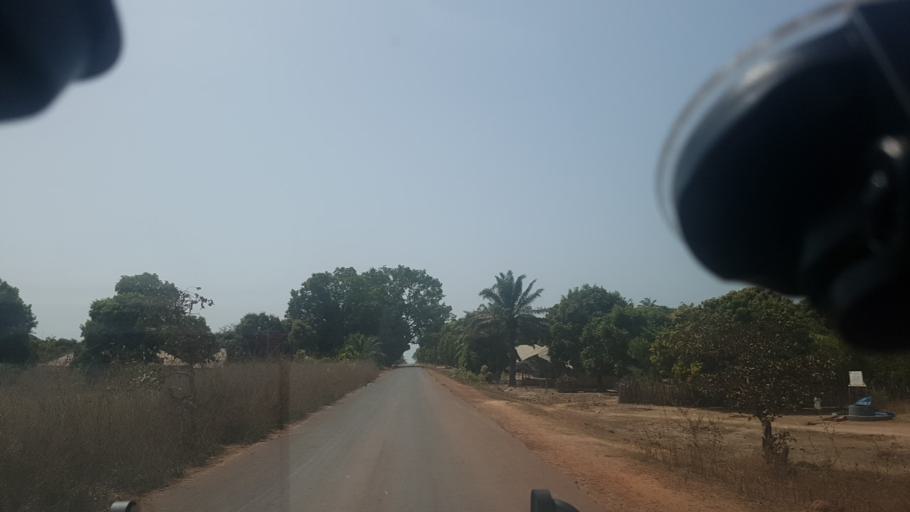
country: GW
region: Cacheu
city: Cacheu
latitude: 12.4101
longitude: -16.0616
